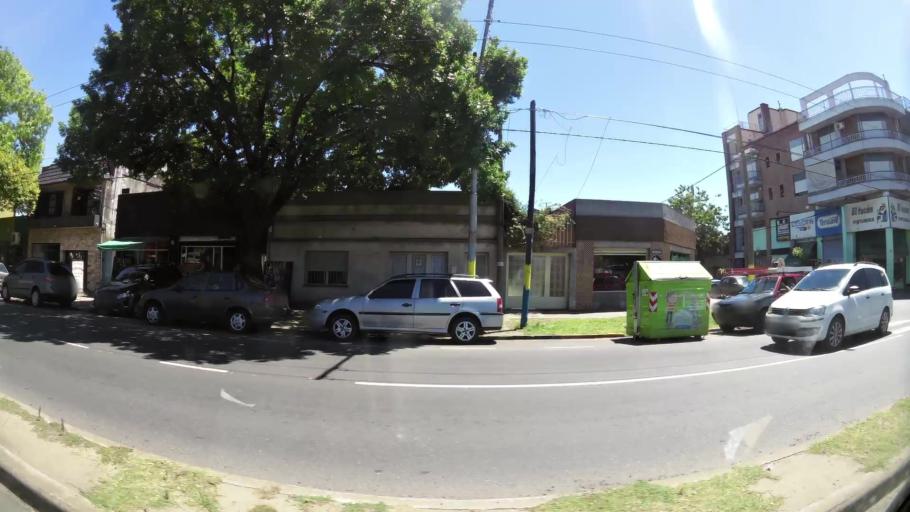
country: AR
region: Santa Fe
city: Perez
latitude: -32.9404
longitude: -60.7186
